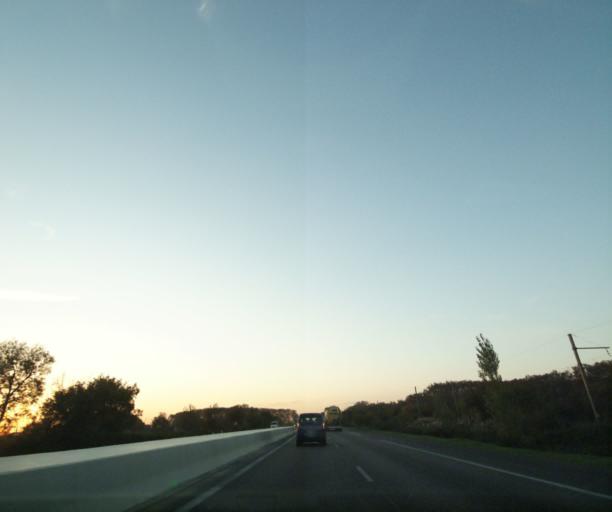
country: FR
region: Provence-Alpes-Cote d'Azur
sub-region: Departement des Bouches-du-Rhone
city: Arles
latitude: 43.6478
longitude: 4.6881
